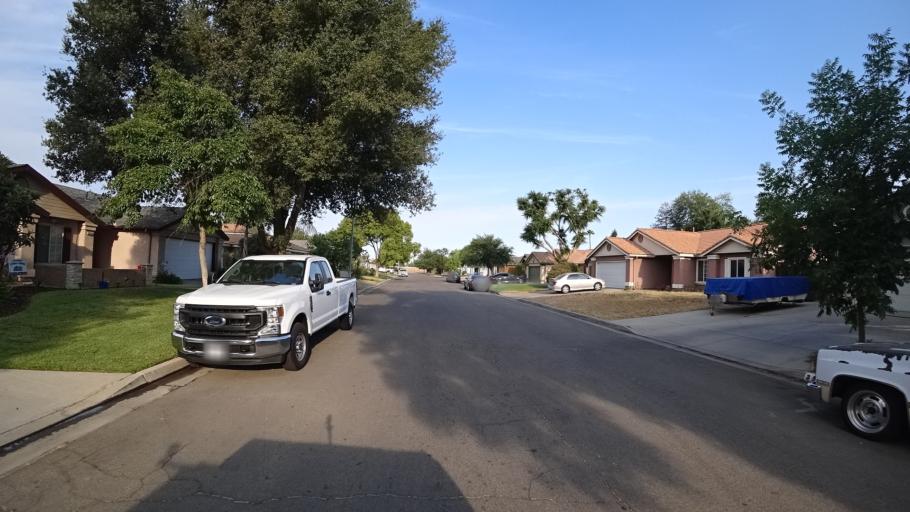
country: US
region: California
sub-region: Fresno County
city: West Park
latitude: 36.7686
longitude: -119.8564
